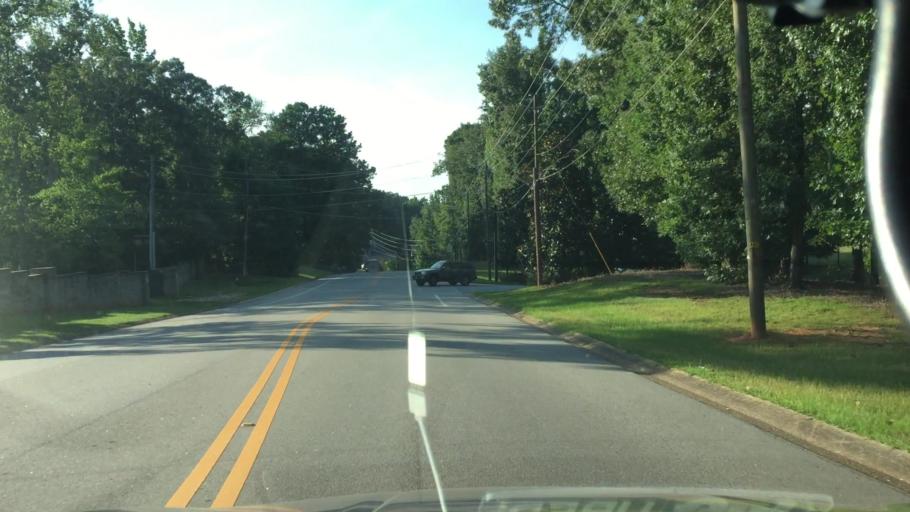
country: US
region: Alabama
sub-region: Lee County
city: Opelika
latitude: 32.5975
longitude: -85.4177
